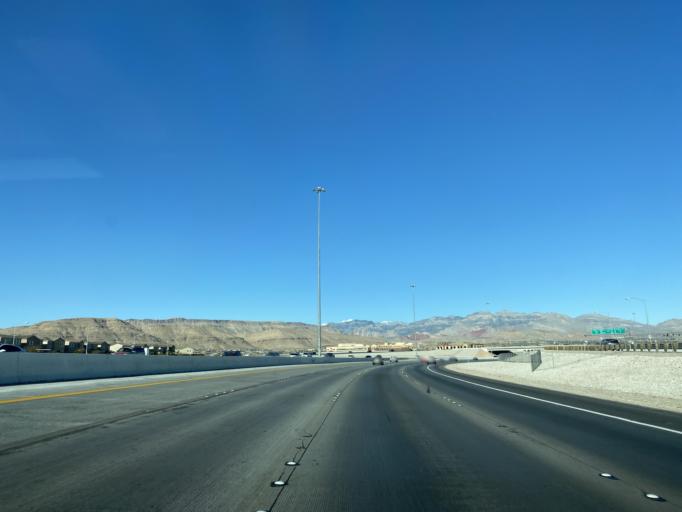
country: US
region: Nevada
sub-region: Clark County
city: Spring Valley
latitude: 36.0656
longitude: -115.2854
